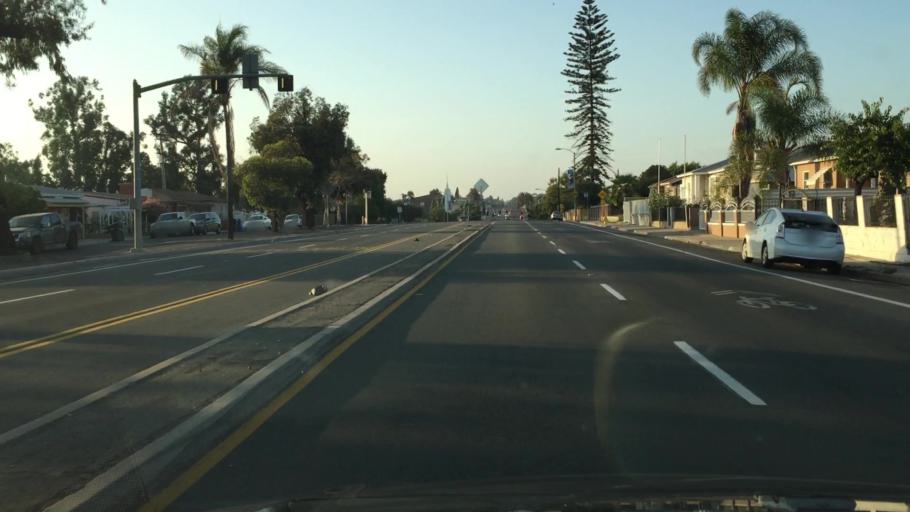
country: US
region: California
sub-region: San Diego County
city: Lemon Grove
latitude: 32.7330
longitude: -117.0797
